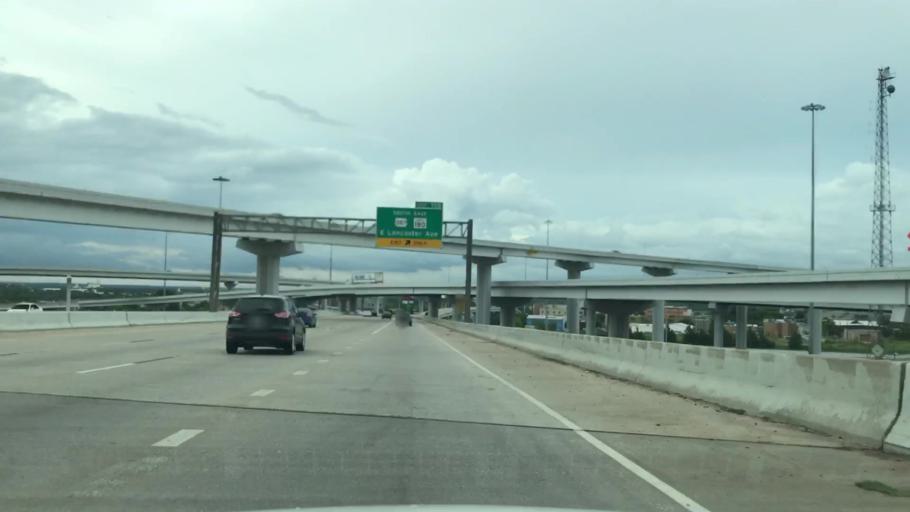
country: US
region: Texas
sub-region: Tarrant County
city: Fort Worth
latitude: 32.7453
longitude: -97.3227
